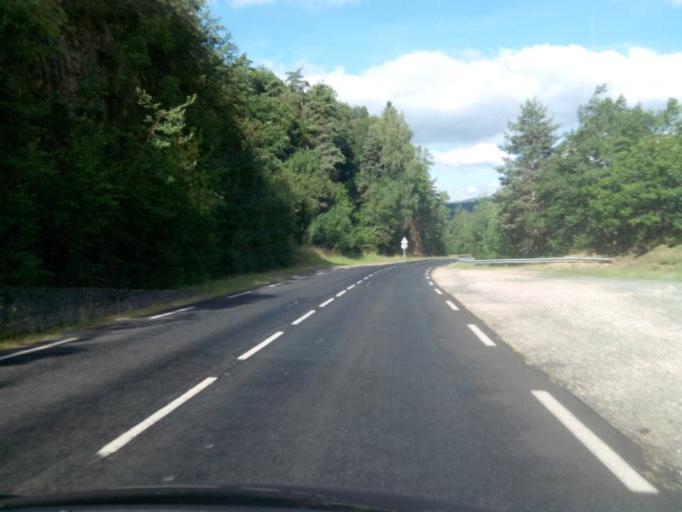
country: FR
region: Auvergne
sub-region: Departement de la Haute-Loire
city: Retournac
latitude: 45.2045
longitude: 4.0114
